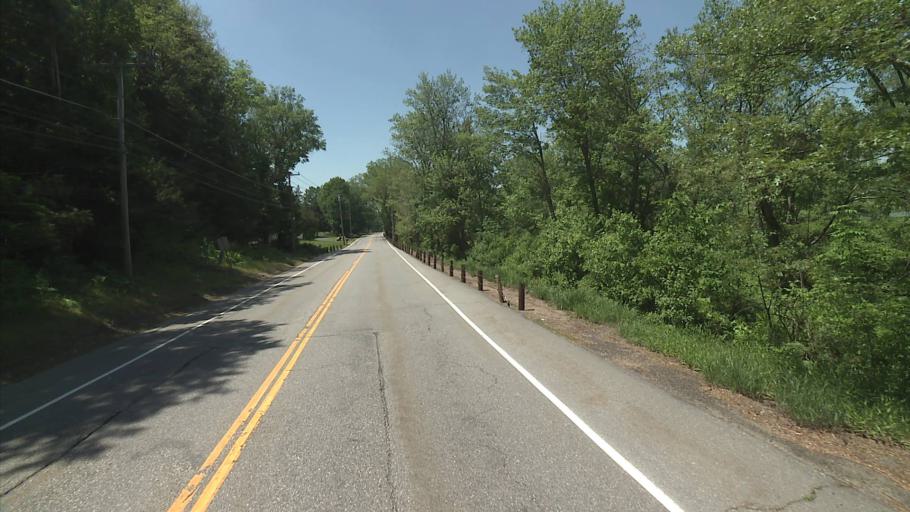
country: US
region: Connecticut
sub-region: Tolland County
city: Stafford
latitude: 41.9932
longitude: -72.2736
